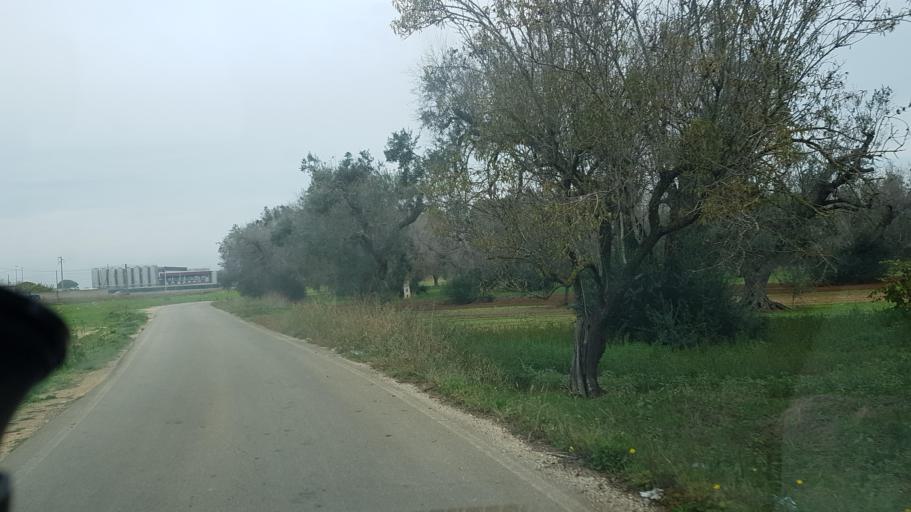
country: IT
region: Apulia
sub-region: Provincia di Brindisi
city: Cellino San Marco
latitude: 40.4771
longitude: 17.9679
